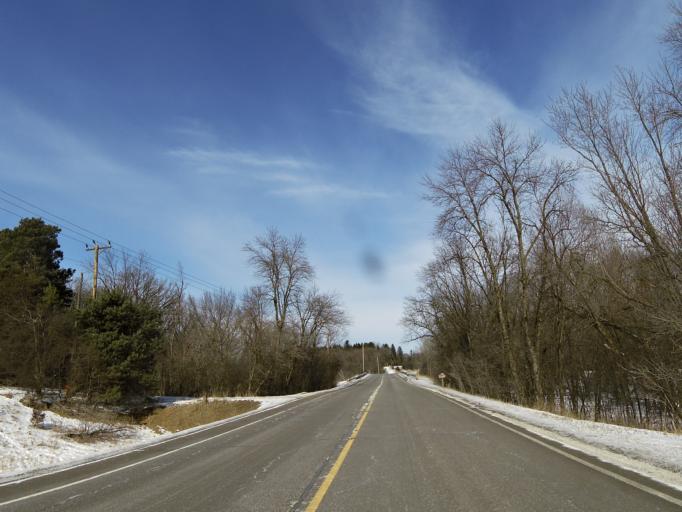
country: US
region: Minnesota
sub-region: Washington County
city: Afton
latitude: 44.9099
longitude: -92.7806
